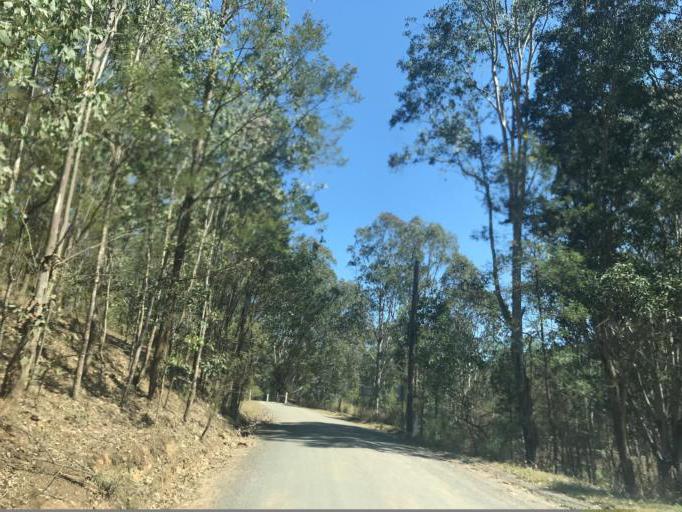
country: AU
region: New South Wales
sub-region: Hornsby Shire
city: Glenorie
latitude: -33.2582
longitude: 150.9750
